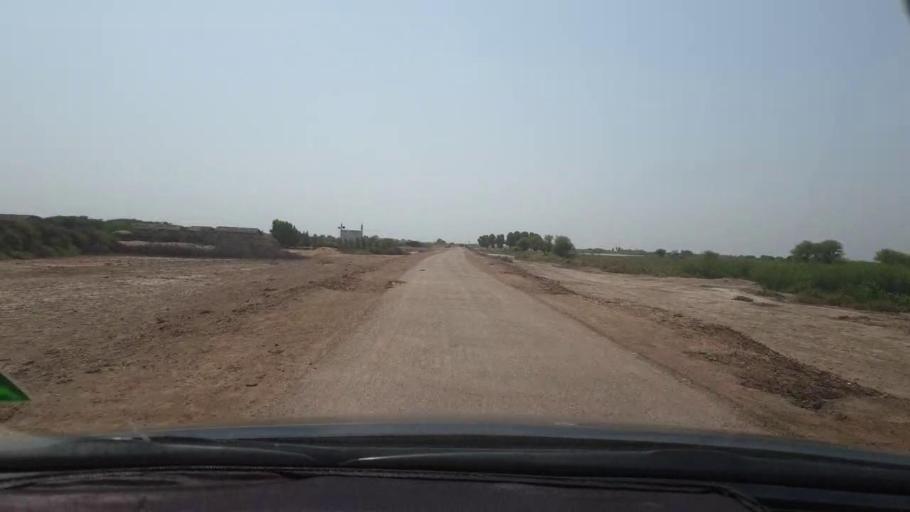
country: PK
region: Sindh
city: Tando Bago
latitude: 24.8000
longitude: 69.1684
